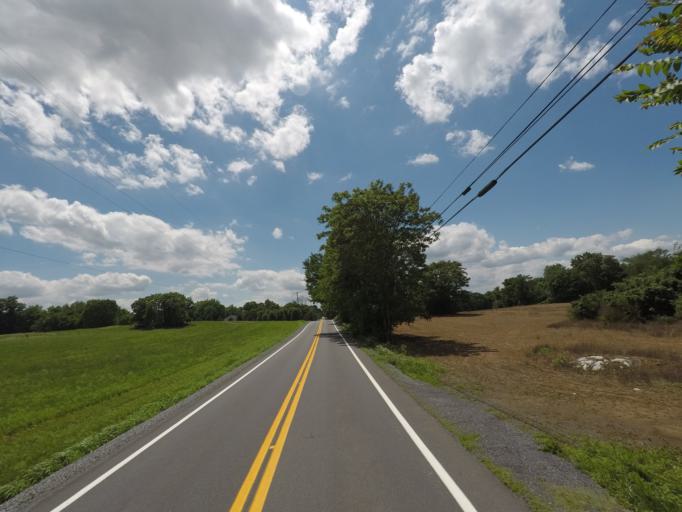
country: US
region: West Virginia
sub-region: Jefferson County
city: Shepherdstown
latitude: 39.4034
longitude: -77.8644
